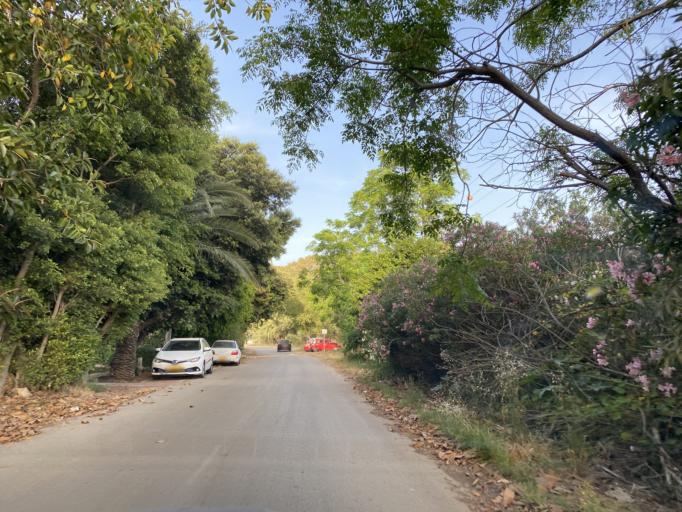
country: IL
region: Tel Aviv
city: Herzliyya
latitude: 32.1547
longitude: 34.8299
